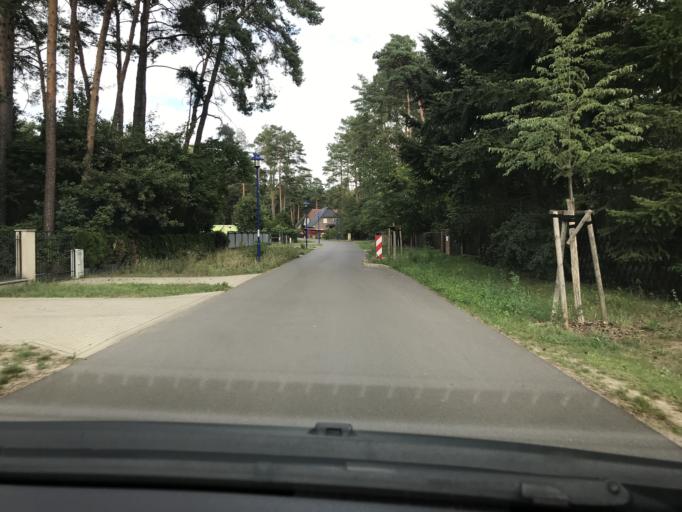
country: DE
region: Brandenburg
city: Wandlitz
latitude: 52.7113
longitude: 13.4446
